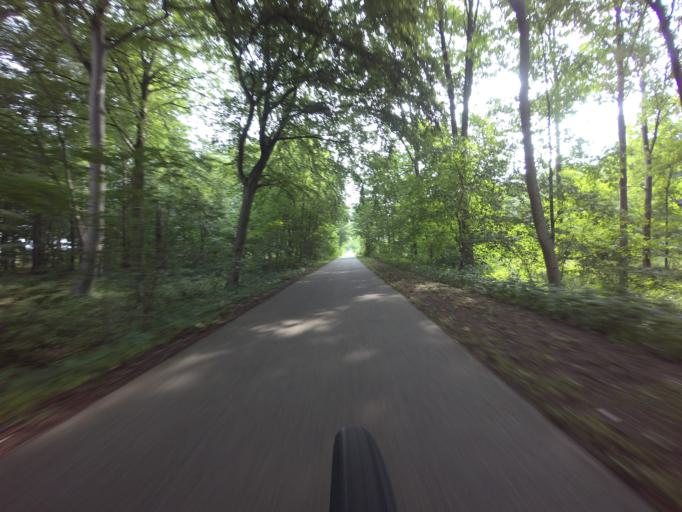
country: DK
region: Zealand
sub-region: Naestved Kommune
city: Naestved
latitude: 55.2511
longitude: 11.7438
